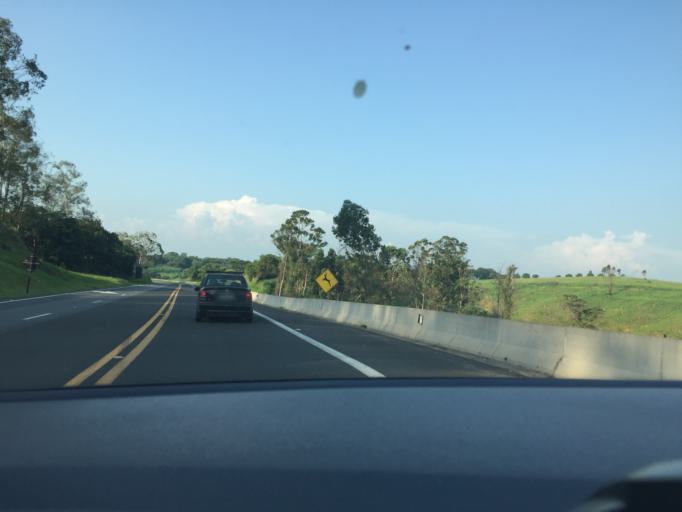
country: BR
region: Sao Paulo
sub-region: Louveira
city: Louveira
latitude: -23.0688
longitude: -46.9020
